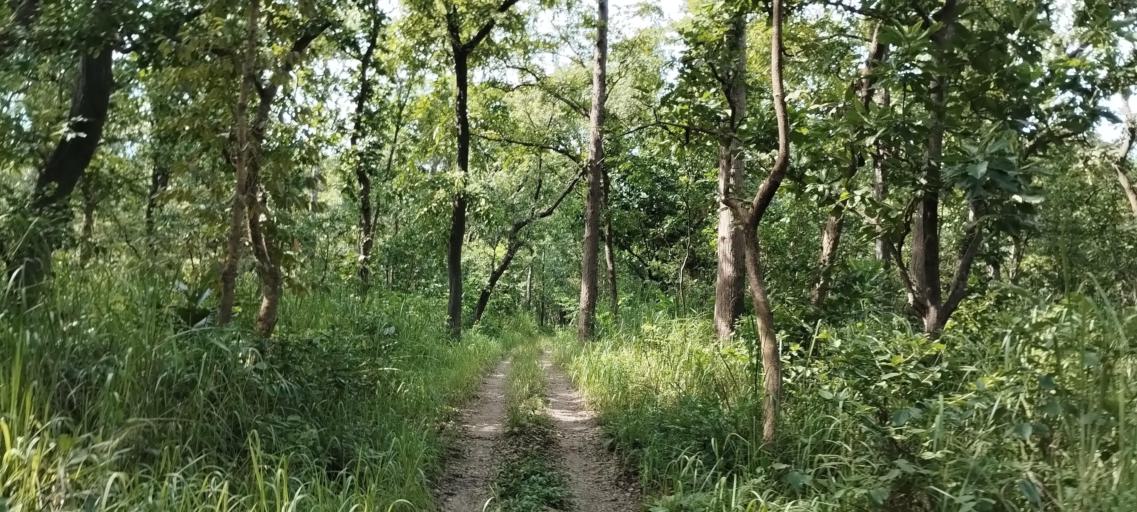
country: NP
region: Far Western
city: Tikapur
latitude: 28.5669
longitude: 81.2922
